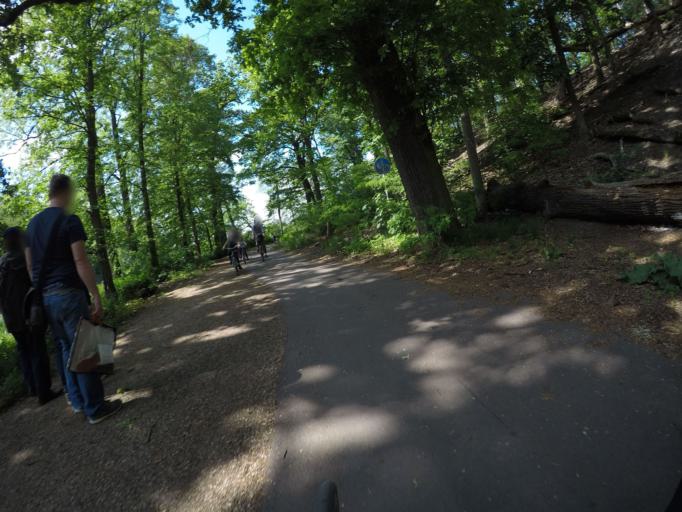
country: DE
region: Brandenburg
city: Potsdam
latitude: 52.4223
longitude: 13.1065
